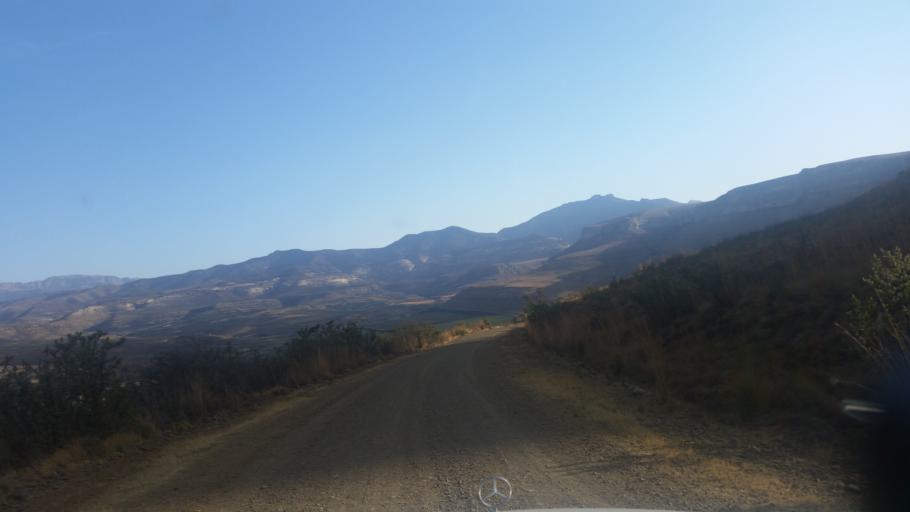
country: ZA
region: Orange Free State
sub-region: Thabo Mofutsanyana District Municipality
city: Phuthaditjhaba
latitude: -28.4910
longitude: 28.6960
